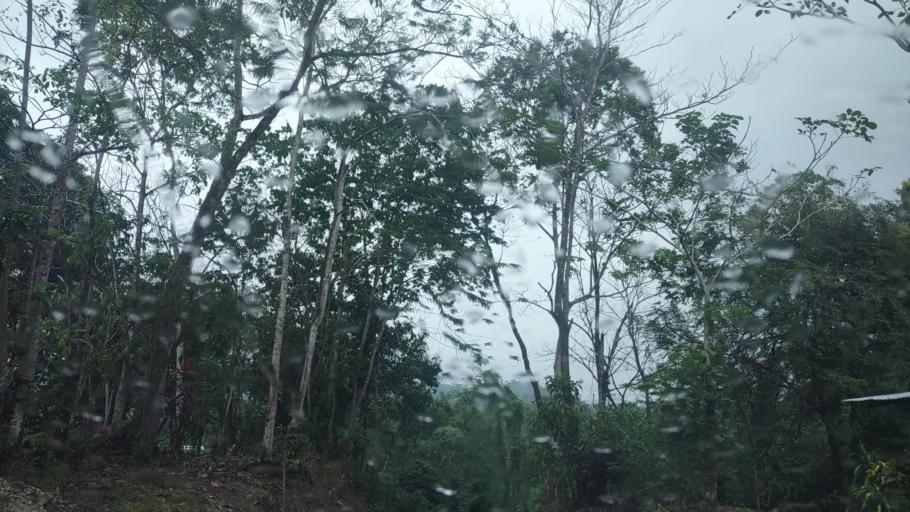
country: MX
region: Veracruz
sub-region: Uxpanapa
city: Poblado 10
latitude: 17.4500
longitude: -94.0962
